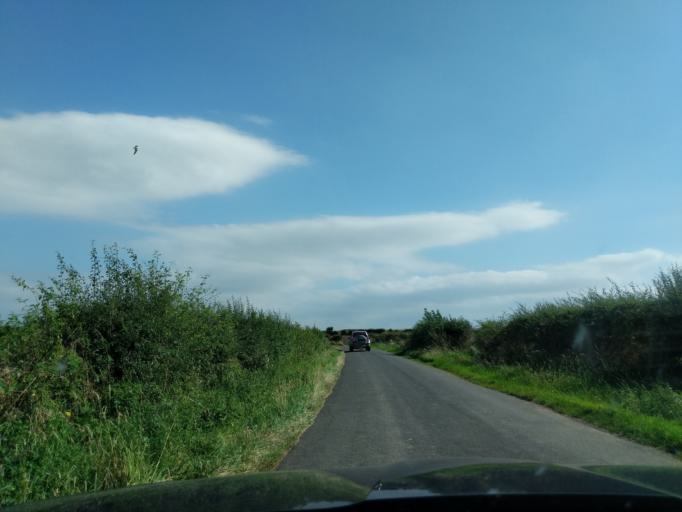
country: GB
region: Scotland
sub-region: The Scottish Borders
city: Coldstream
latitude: 55.6732
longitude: -2.1787
